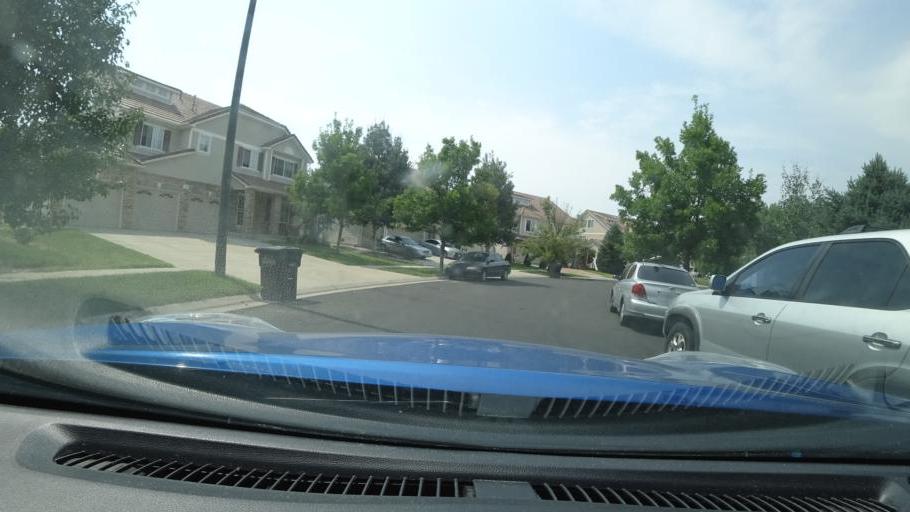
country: US
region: Colorado
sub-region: Adams County
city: Aurora
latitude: 39.7824
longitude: -104.7395
